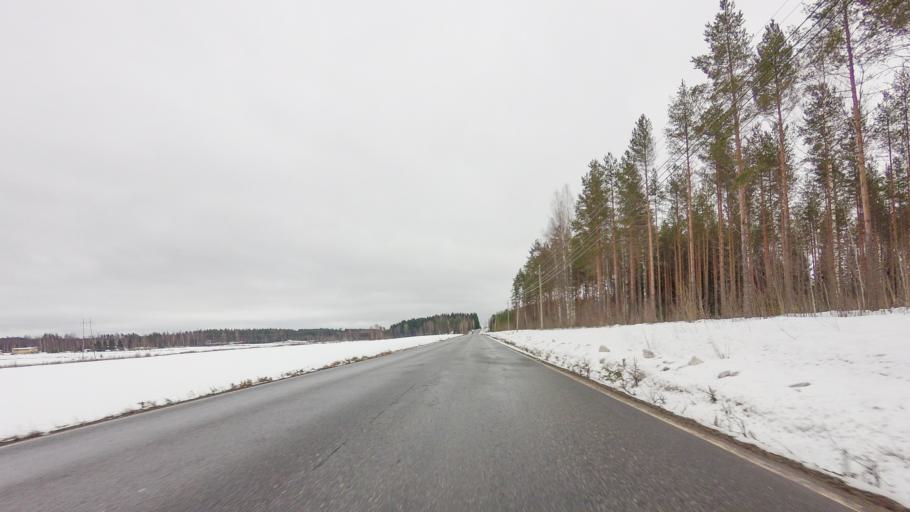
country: FI
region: Southern Savonia
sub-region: Savonlinna
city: Savonlinna
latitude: 61.9529
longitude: 28.8549
